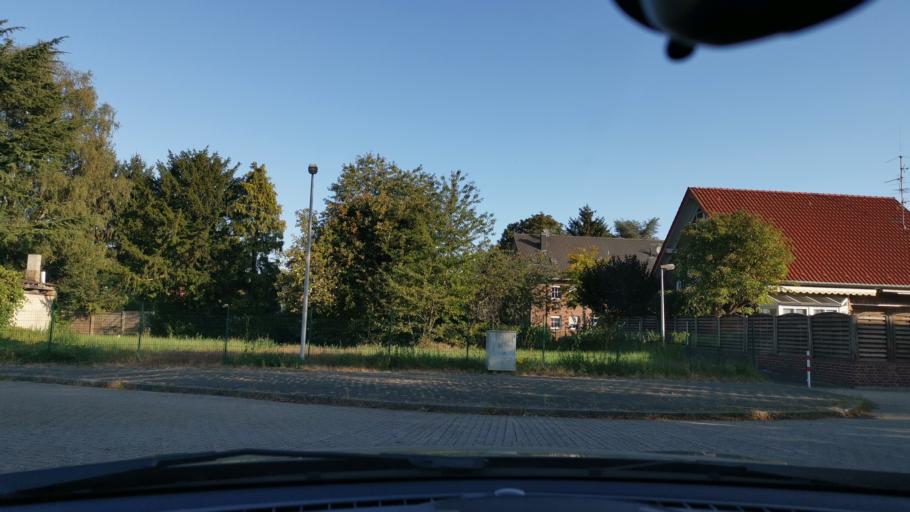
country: DE
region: North Rhine-Westphalia
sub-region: Regierungsbezirk Dusseldorf
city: Dormagen
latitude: 51.1107
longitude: 6.7587
